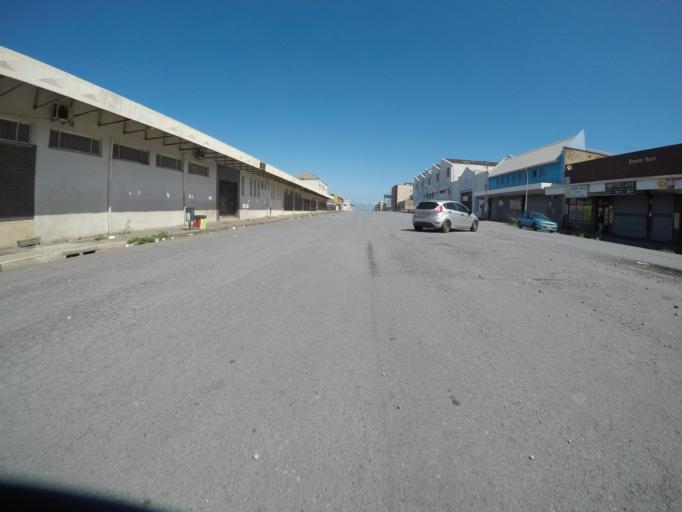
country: ZA
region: Eastern Cape
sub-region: Buffalo City Metropolitan Municipality
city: East London
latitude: -33.0148
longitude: 27.9066
